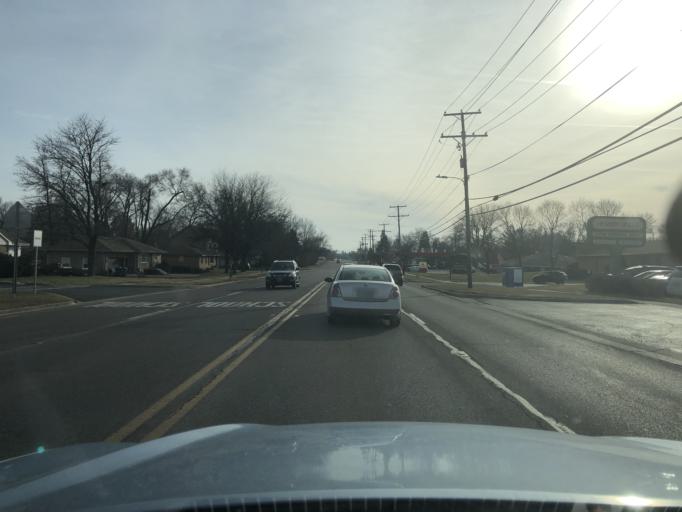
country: US
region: Illinois
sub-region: DuPage County
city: Glendale Heights
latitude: 41.9141
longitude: -88.0814
